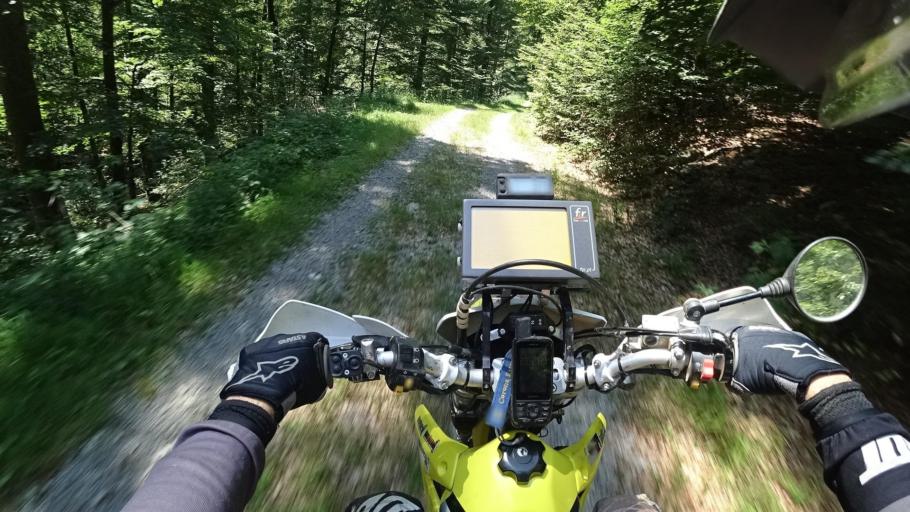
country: HR
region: Primorsko-Goranska
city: Bribir
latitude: 45.2677
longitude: 14.8660
